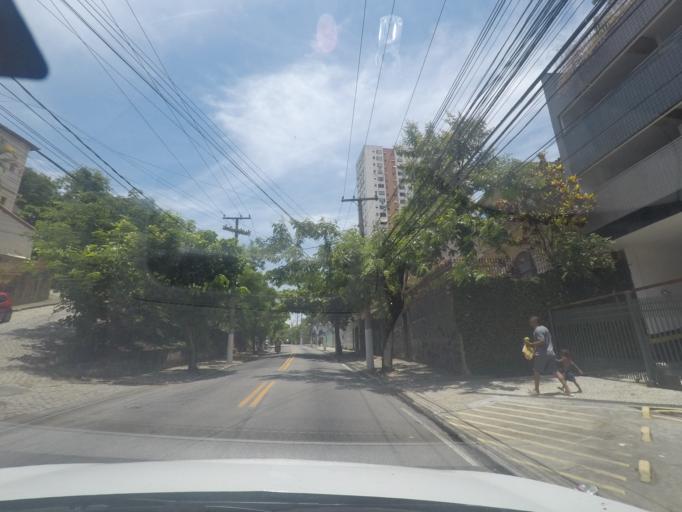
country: BR
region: Rio de Janeiro
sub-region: Niteroi
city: Niteroi
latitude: -22.8999
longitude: -43.1162
